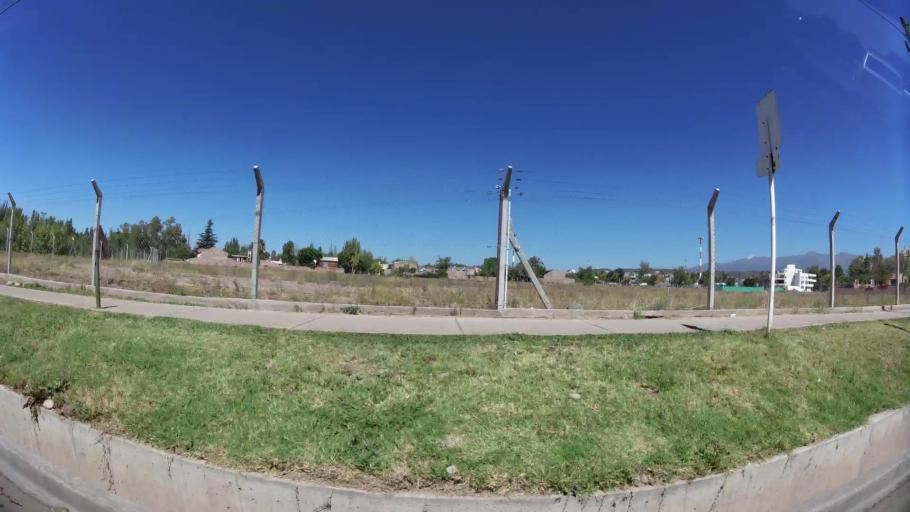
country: AR
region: Mendoza
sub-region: Departamento de Godoy Cruz
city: Godoy Cruz
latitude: -32.9542
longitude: -68.8525
